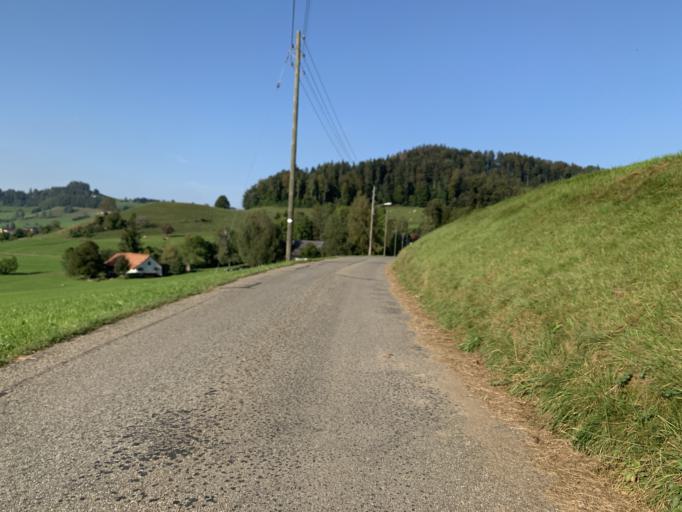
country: CH
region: Zurich
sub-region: Bezirk Hinwil
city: Baretswil
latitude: 47.3211
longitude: 8.8760
